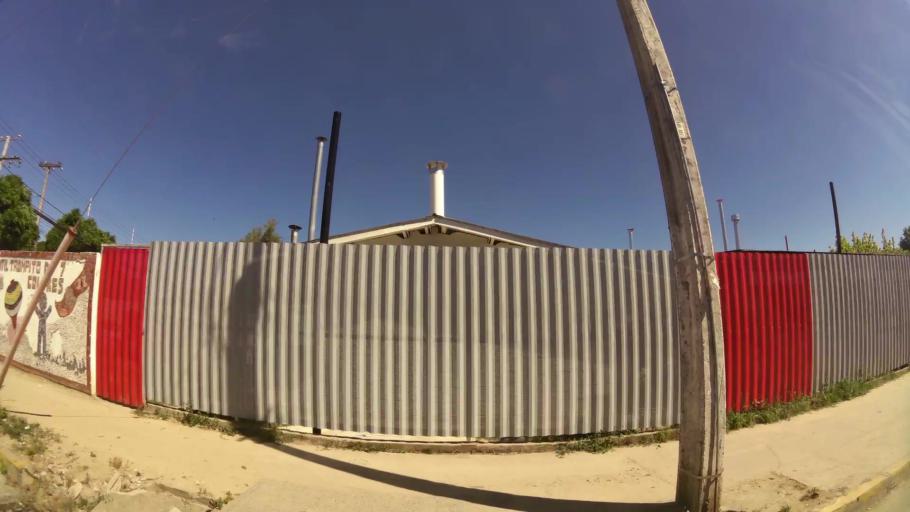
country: CL
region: Valparaiso
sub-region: Provincia de Marga Marga
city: Quilpue
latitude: -33.3213
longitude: -71.4024
